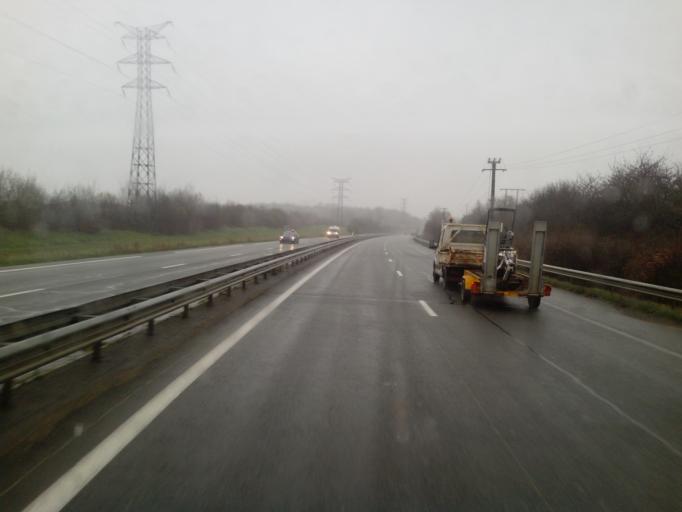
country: FR
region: Poitou-Charentes
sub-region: Departement de la Vienne
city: Mignaloux-Beauvoir
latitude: 46.5577
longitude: 0.3982
